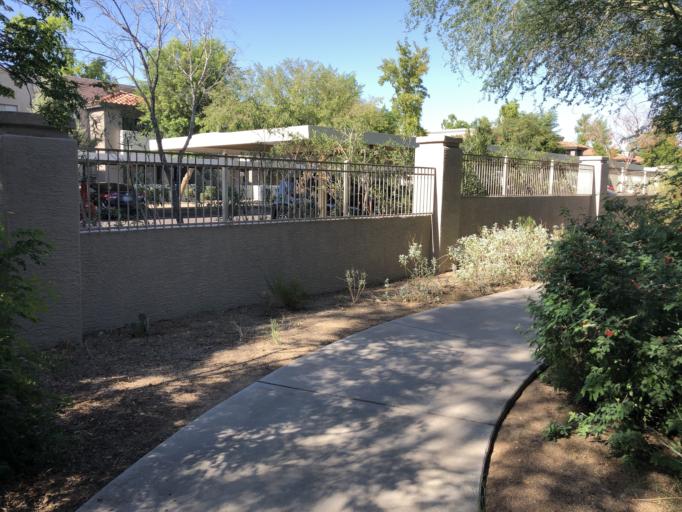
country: US
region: Arizona
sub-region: Maricopa County
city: Guadalupe
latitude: 33.3128
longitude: -111.9232
